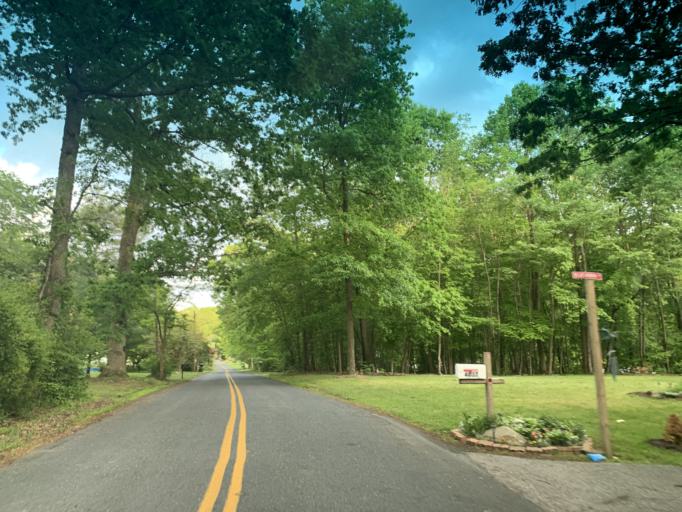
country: US
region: Pennsylvania
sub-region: York County
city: Susquehanna Trails
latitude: 39.6772
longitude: -76.2445
